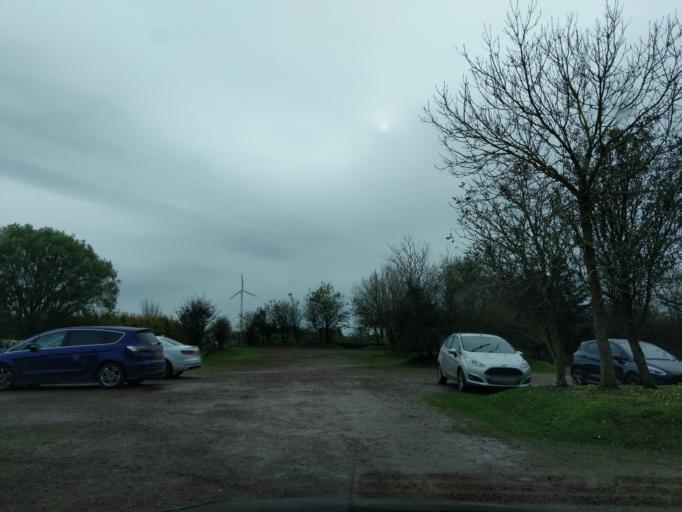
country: GB
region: Scotland
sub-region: Dumfries and Galloway
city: Kirkcudbright
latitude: 54.8412
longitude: -4.1833
